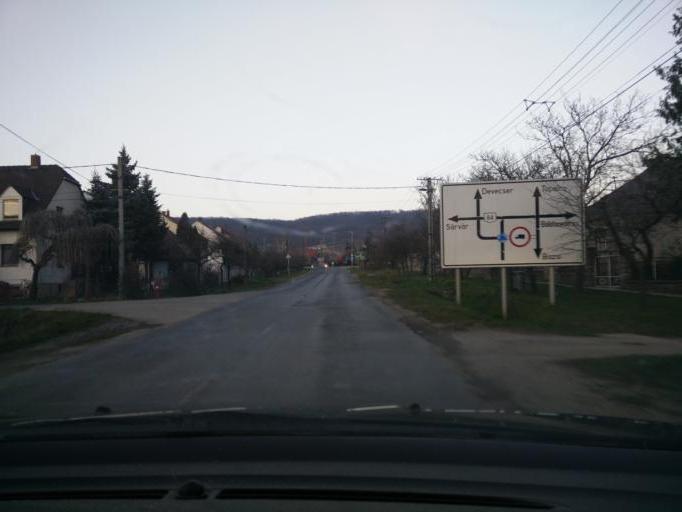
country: HU
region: Veszprem
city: Sumeg
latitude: 46.9844
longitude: 17.2737
